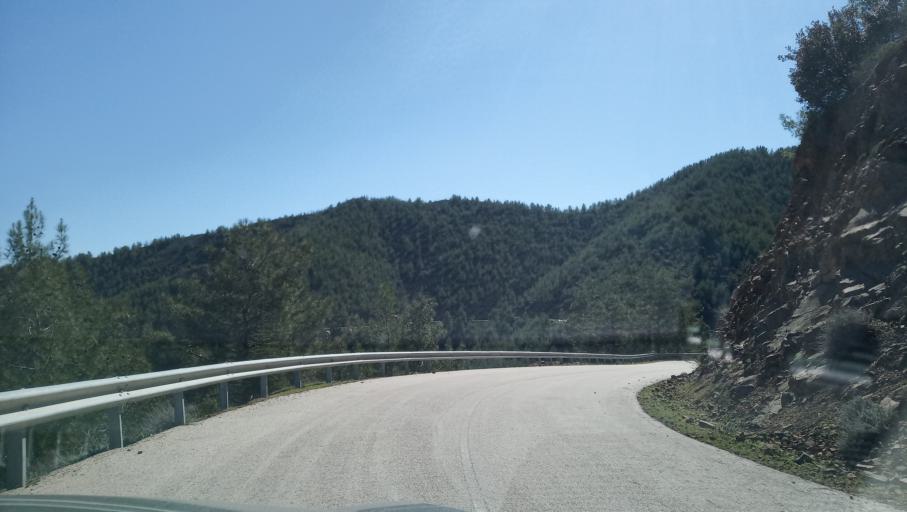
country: CY
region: Lefkosia
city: Lefka
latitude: 35.0720
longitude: 32.7543
